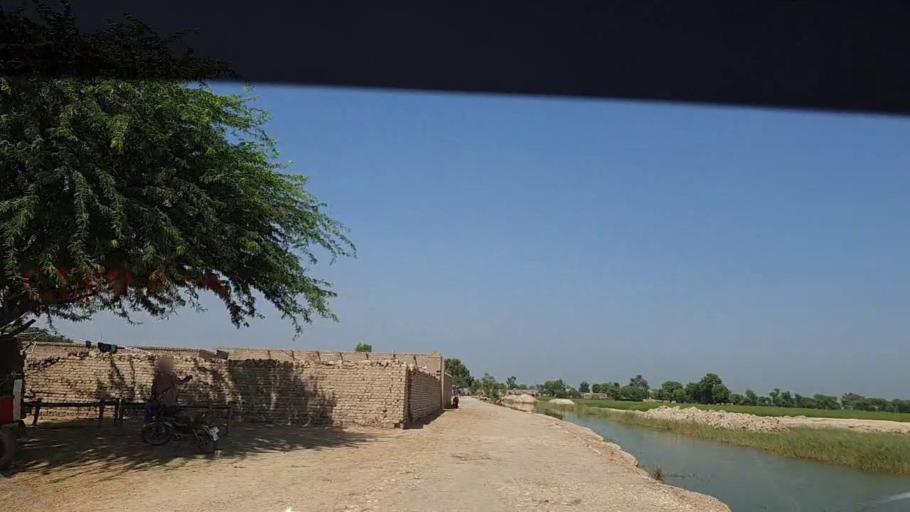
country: PK
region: Sindh
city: Tangwani
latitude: 28.2819
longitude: 69.0369
